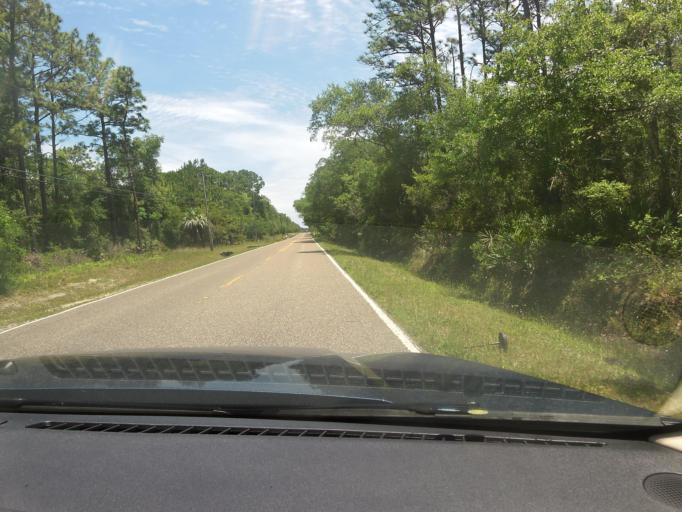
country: US
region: Florida
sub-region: Duval County
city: Atlantic Beach
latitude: 30.4580
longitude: -81.5145
